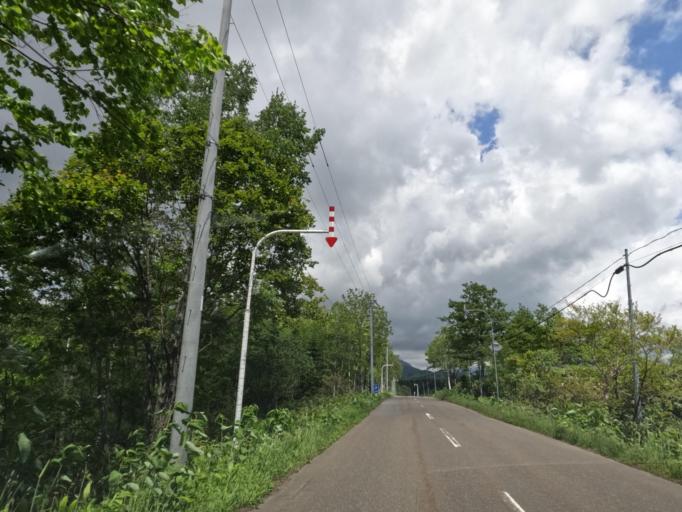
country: JP
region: Hokkaido
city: Tobetsu
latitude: 43.4494
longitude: 141.5862
